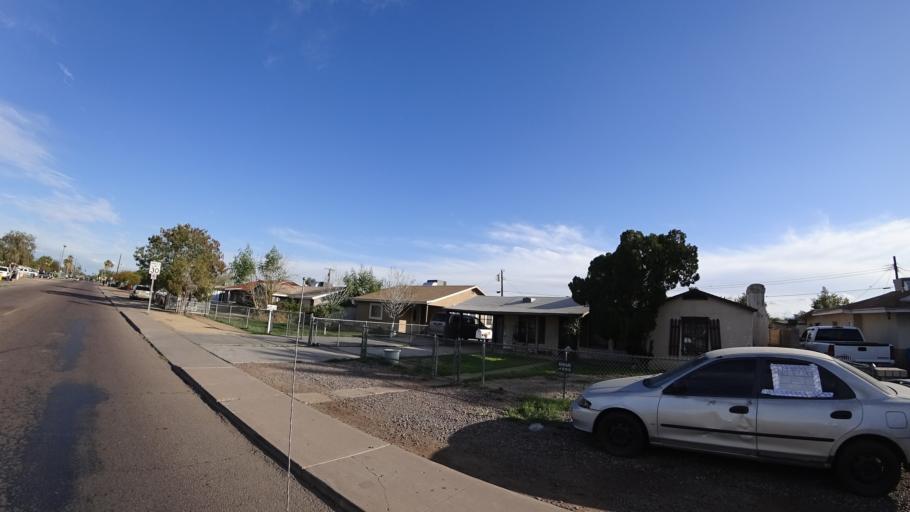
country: US
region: Arizona
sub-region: Maricopa County
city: Phoenix
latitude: 33.4586
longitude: -112.1383
